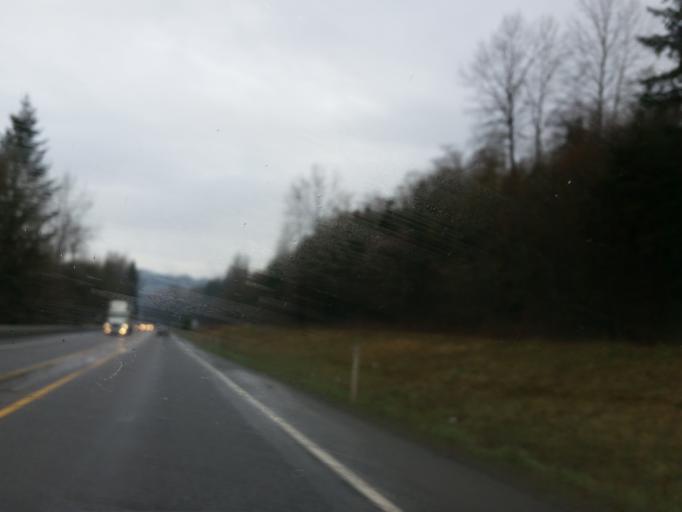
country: US
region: Washington
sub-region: Snohomish County
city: Cathcart
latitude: 47.8198
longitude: -122.0633
